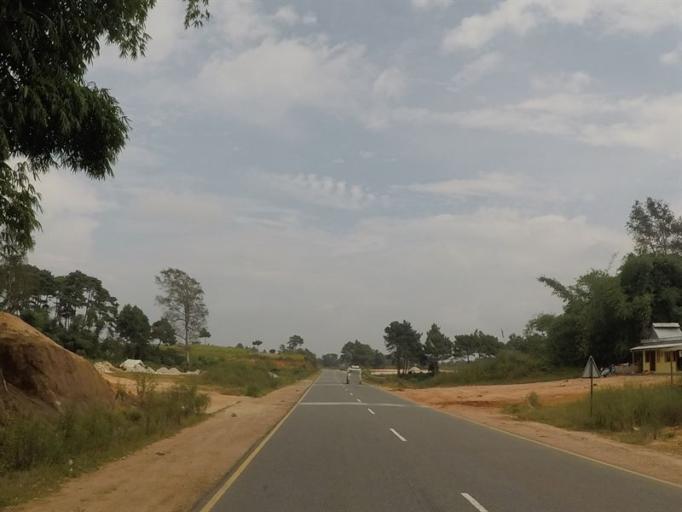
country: IN
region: Meghalaya
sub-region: East Khasi Hills
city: Shillong
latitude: 25.4909
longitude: 92.1843
